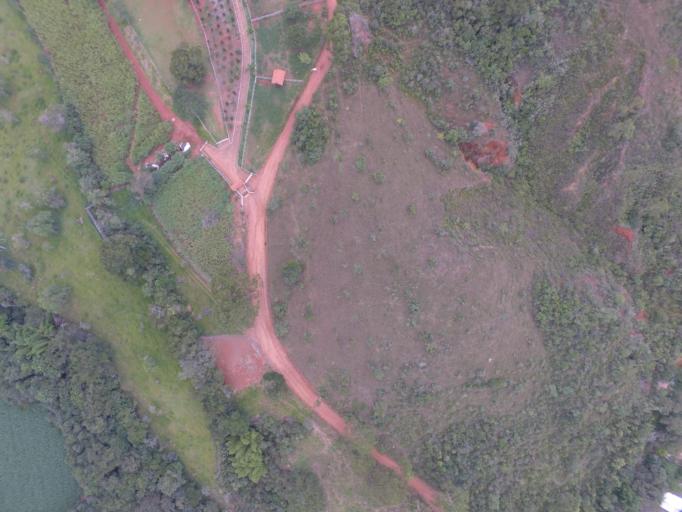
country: BR
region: Minas Gerais
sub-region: Tiradentes
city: Tiradentes
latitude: -21.0476
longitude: -44.0885
